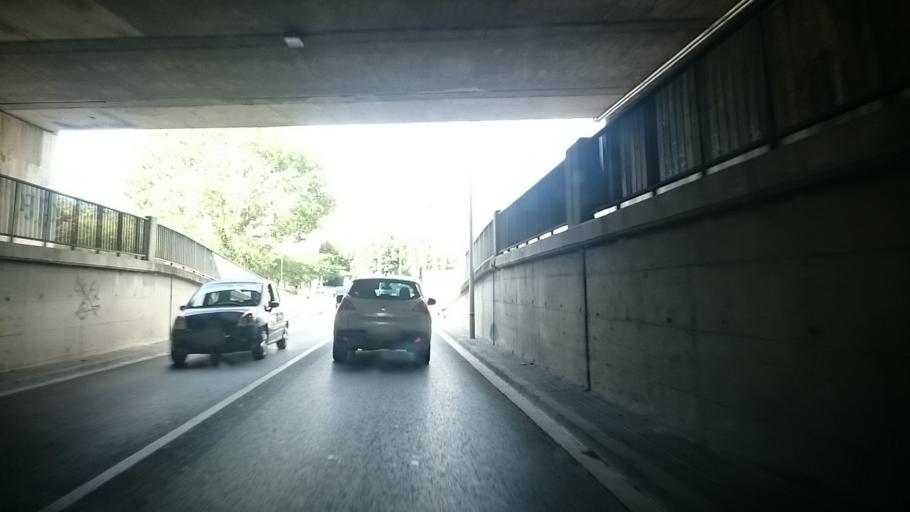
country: ES
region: Catalonia
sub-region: Provincia de Barcelona
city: Igualada
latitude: 41.5894
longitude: 1.6155
